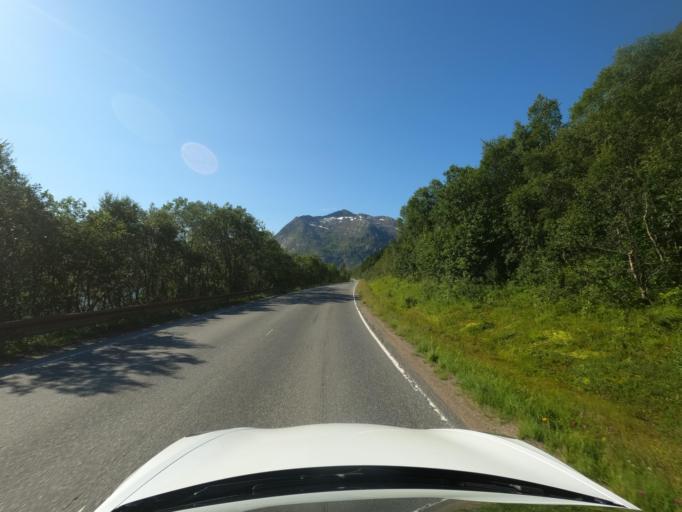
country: NO
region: Nordland
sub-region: Lodingen
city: Lodingen
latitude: 68.5524
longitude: 15.7513
